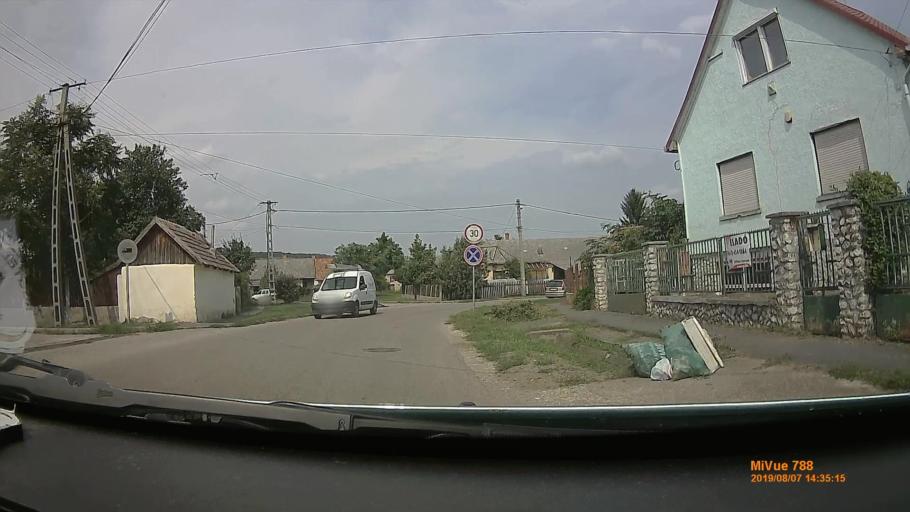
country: HU
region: Borsod-Abauj-Zemplen
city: Szikszo
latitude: 48.2053
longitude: 20.9269
